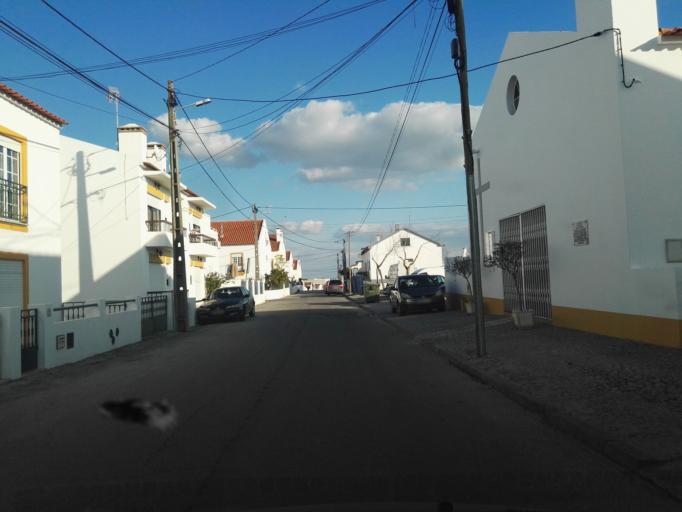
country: PT
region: Evora
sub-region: Evora
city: Evora
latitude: 38.5534
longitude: -7.9272
